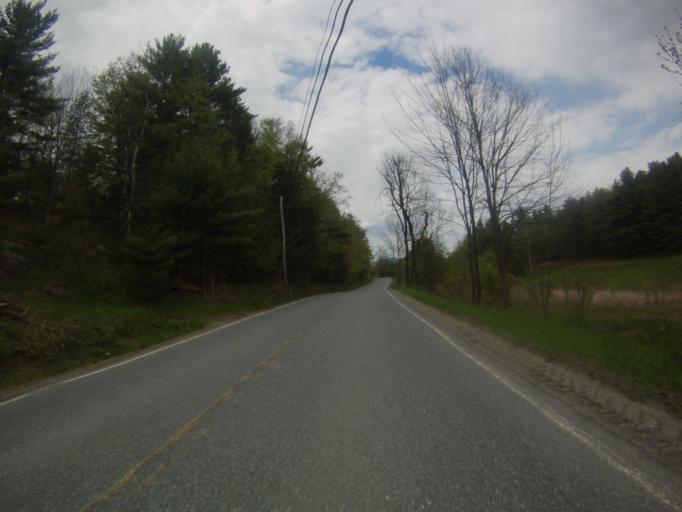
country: US
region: New York
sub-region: Essex County
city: Port Henry
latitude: 43.9877
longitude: -73.4909
